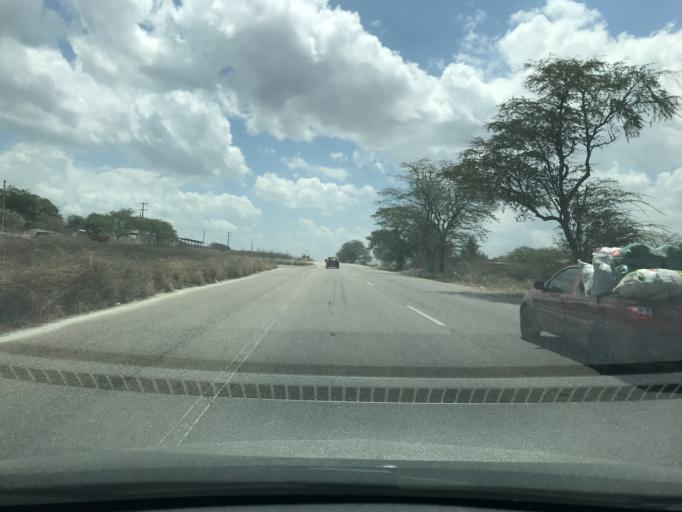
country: BR
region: Pernambuco
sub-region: Caruaru
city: Caruaru
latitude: -8.2954
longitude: -35.8890
